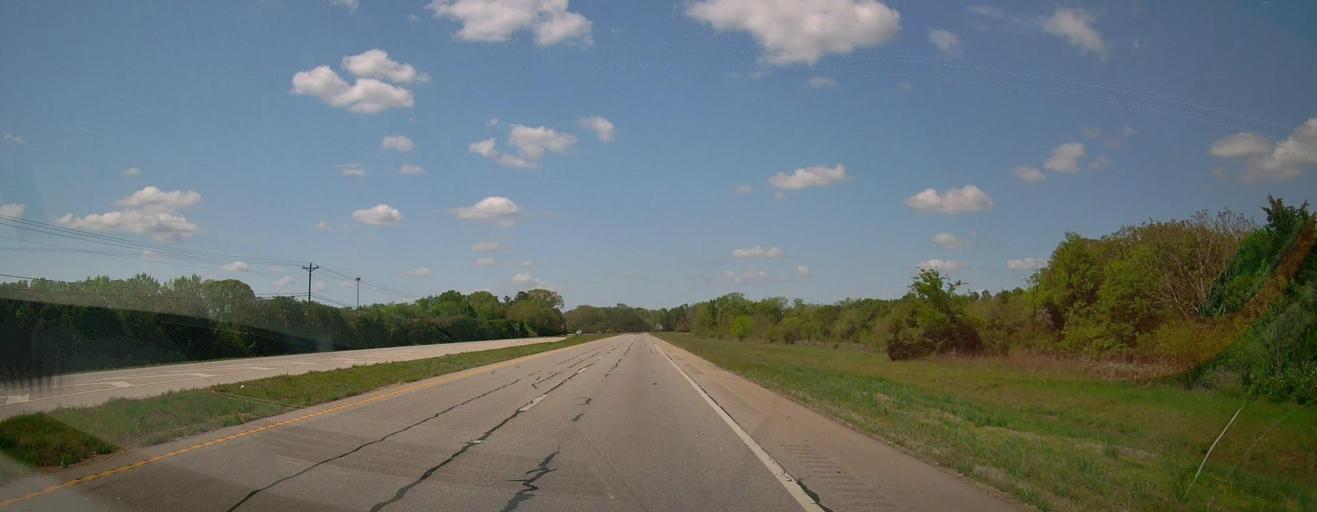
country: US
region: Georgia
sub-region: Putnam County
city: Eatonton
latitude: 33.2634
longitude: -83.3336
